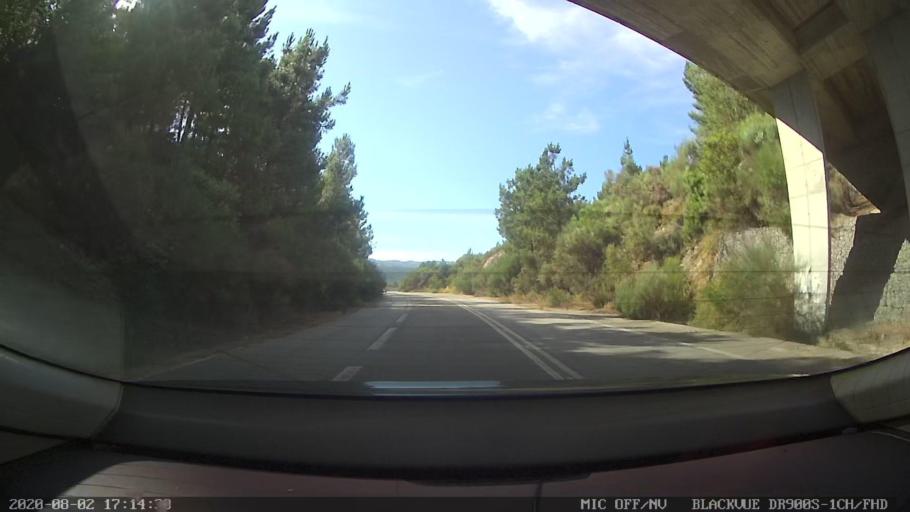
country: PT
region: Vila Real
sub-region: Sabrosa
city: Sabrosa
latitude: 41.3587
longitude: -7.5894
